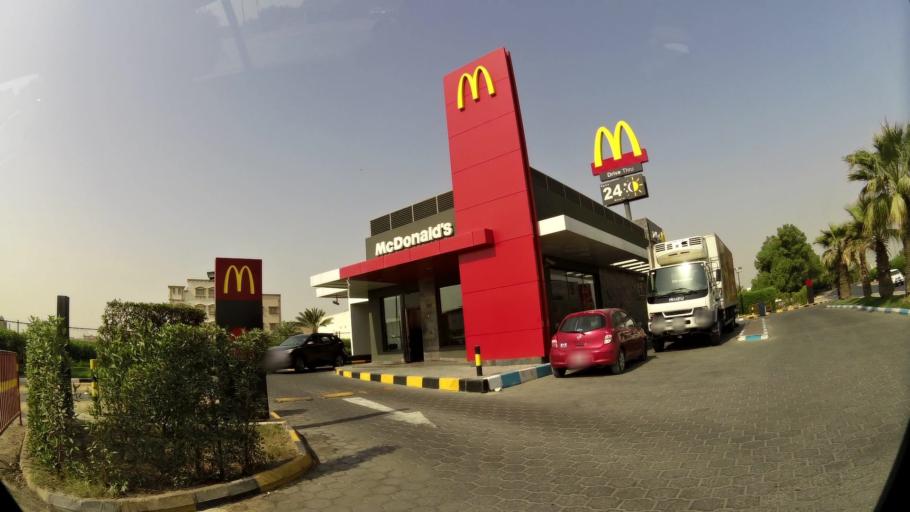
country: KW
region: Al Asimah
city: Ar Rabiyah
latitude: 29.2877
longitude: 47.8805
